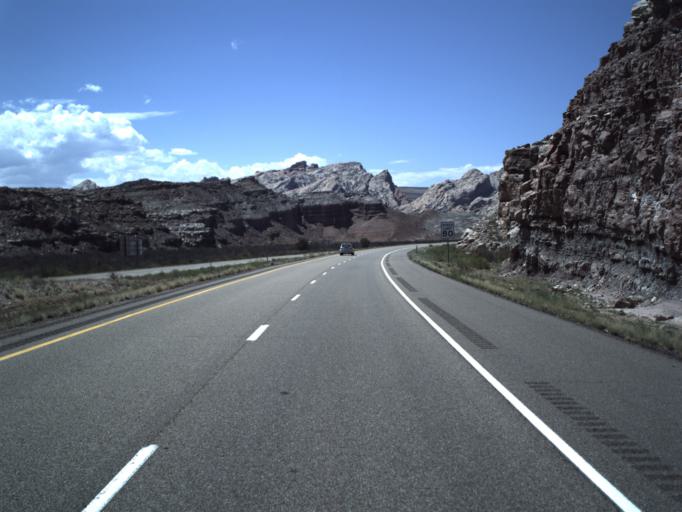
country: US
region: Utah
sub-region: Carbon County
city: East Carbon City
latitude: 38.9215
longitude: -110.3899
